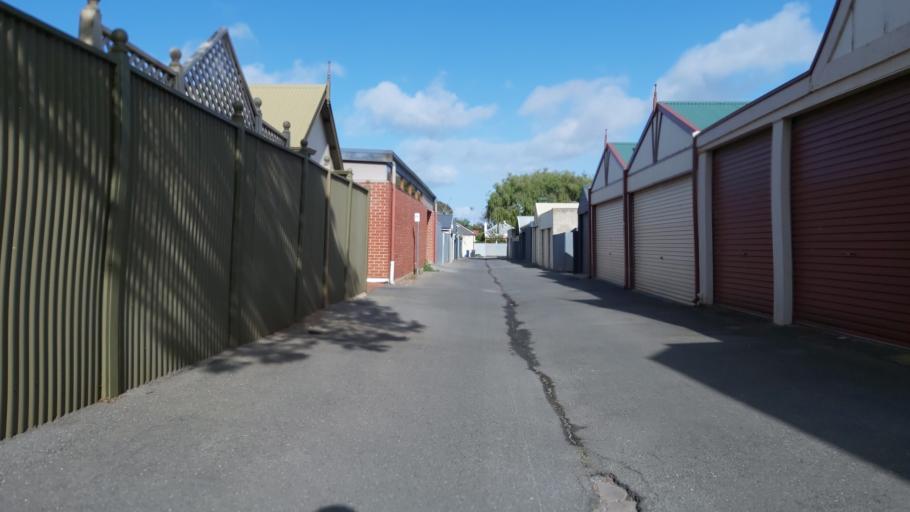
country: AU
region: South Australia
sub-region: Unley
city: Unley
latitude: -34.9434
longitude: 138.5944
